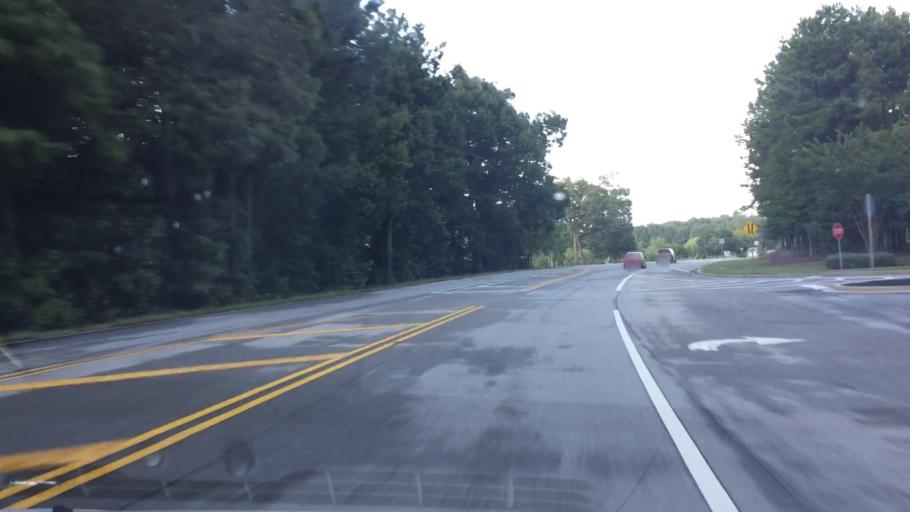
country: US
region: Georgia
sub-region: Clayton County
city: Lovejoy
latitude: 33.4385
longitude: -84.2696
